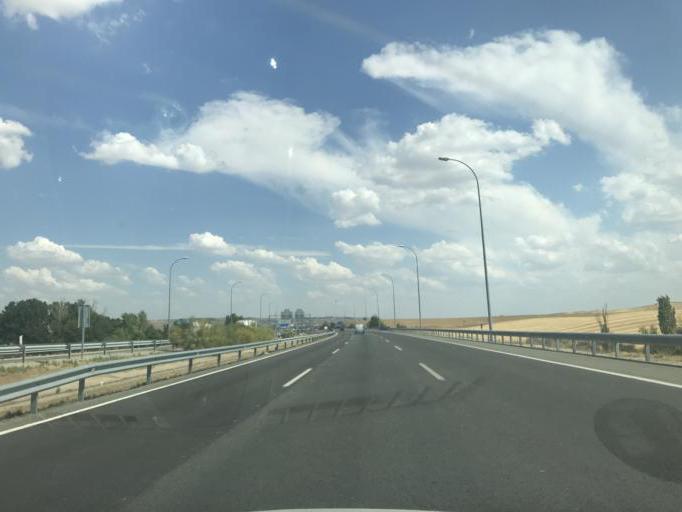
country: ES
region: Madrid
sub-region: Provincia de Madrid
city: San Sebastian de los Reyes
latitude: 40.5575
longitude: -3.5893
